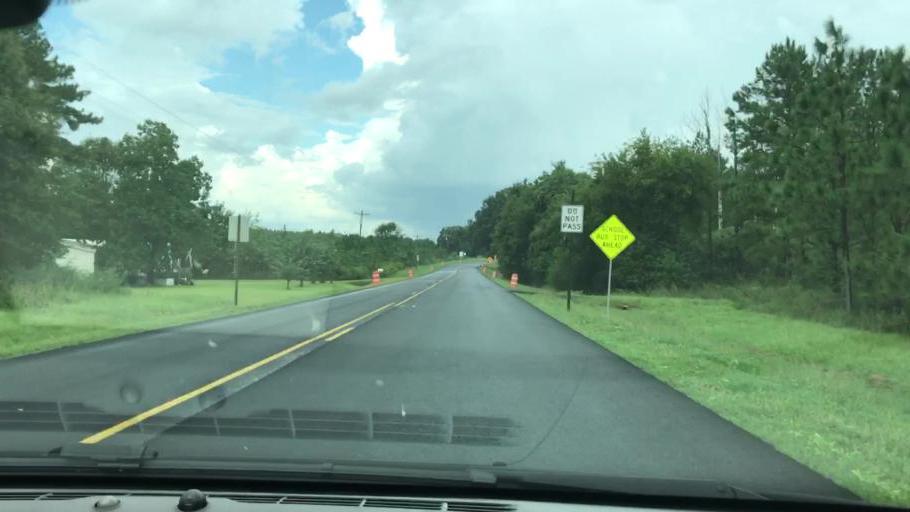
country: US
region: Georgia
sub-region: Early County
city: Blakely
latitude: 31.4132
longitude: -84.9621
